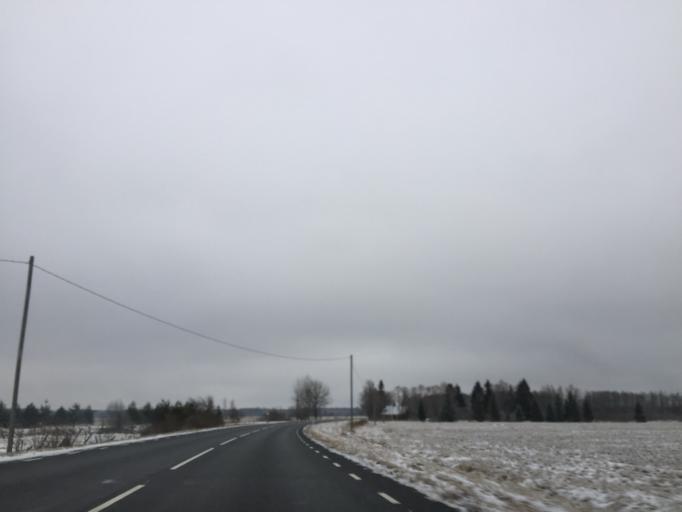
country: EE
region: Laeaene
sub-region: Lihula vald
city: Lihula
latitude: 58.6678
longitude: 23.8322
